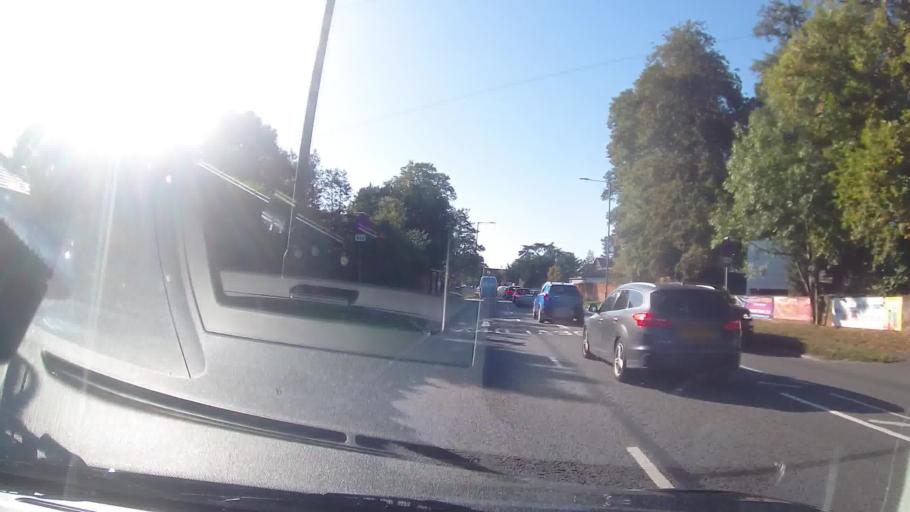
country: GB
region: England
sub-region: Buckinghamshire
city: Beaconsfield
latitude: 51.6018
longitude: -0.6303
